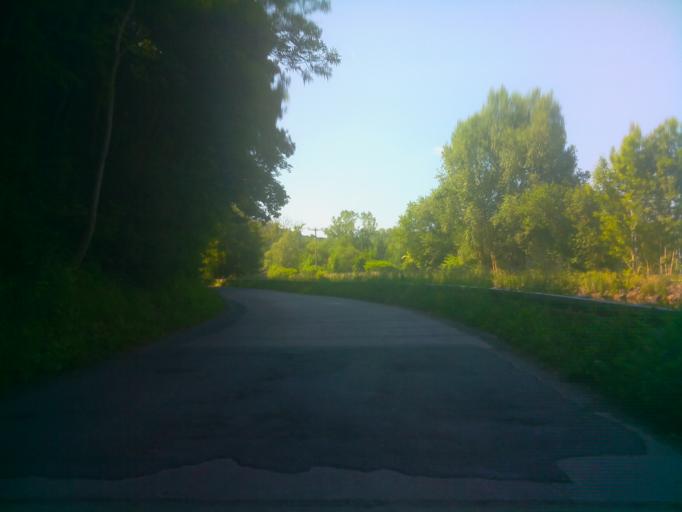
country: DE
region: Thuringia
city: Rudolstadt
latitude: 50.6899
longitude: 11.3377
